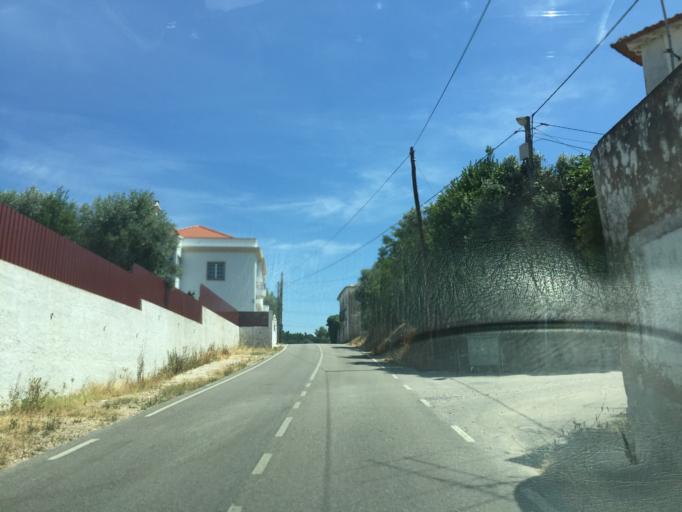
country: PT
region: Santarem
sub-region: Tomar
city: Tomar
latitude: 39.5962
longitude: -8.3226
